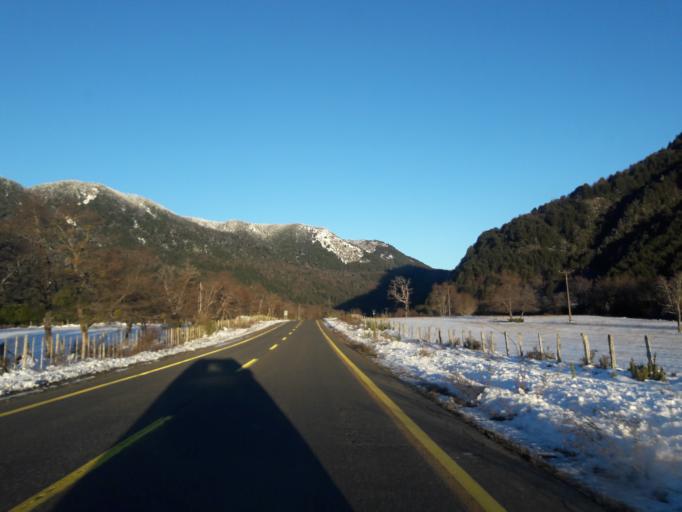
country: CL
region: Araucania
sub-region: Provincia de Cautin
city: Vilcun
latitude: -38.4835
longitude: -71.5333
